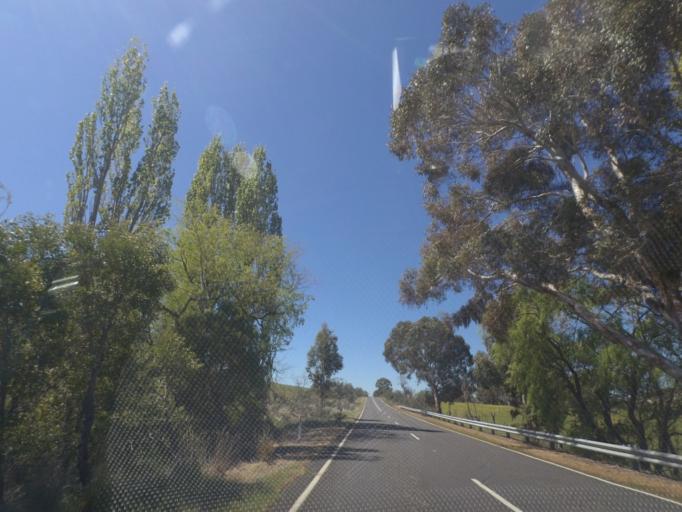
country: AU
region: Victoria
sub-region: Hume
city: Sunbury
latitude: -37.1682
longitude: 144.7561
